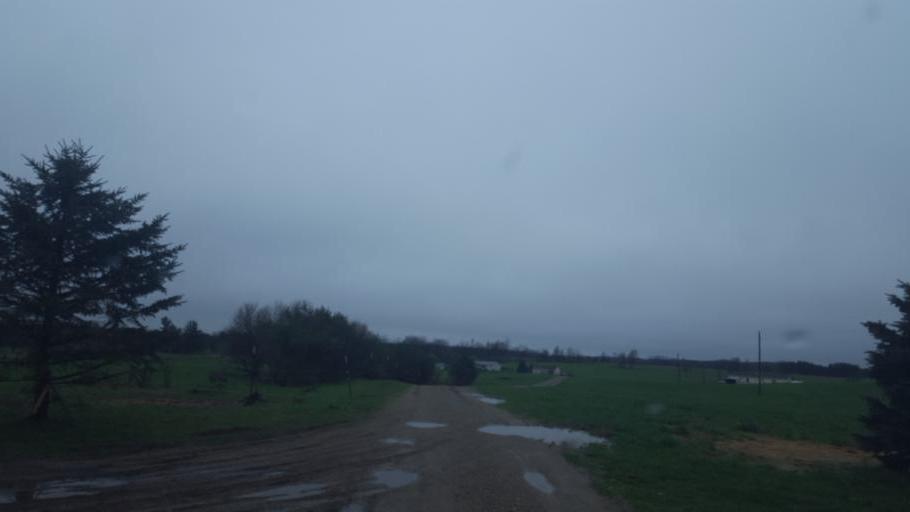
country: US
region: Michigan
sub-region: Isabella County
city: Lake Isabella
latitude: 43.5775
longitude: -85.0219
